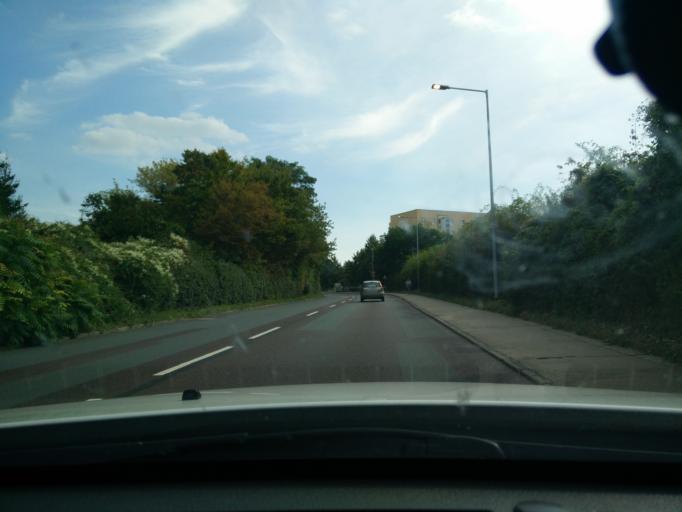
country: DE
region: Saxony-Anhalt
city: Burg bei Magdeburg
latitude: 52.2664
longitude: 11.8409
